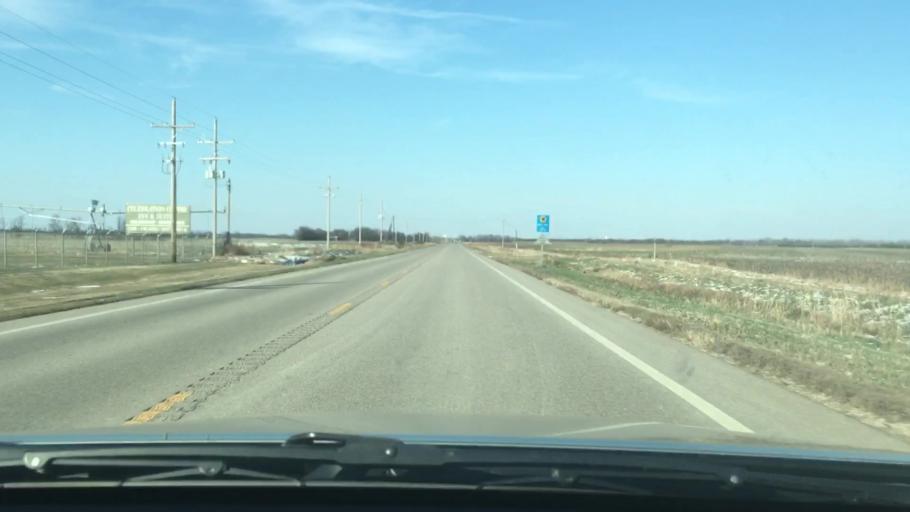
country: US
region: Kansas
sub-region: Rice County
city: Lyons
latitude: 38.2781
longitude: -98.2019
